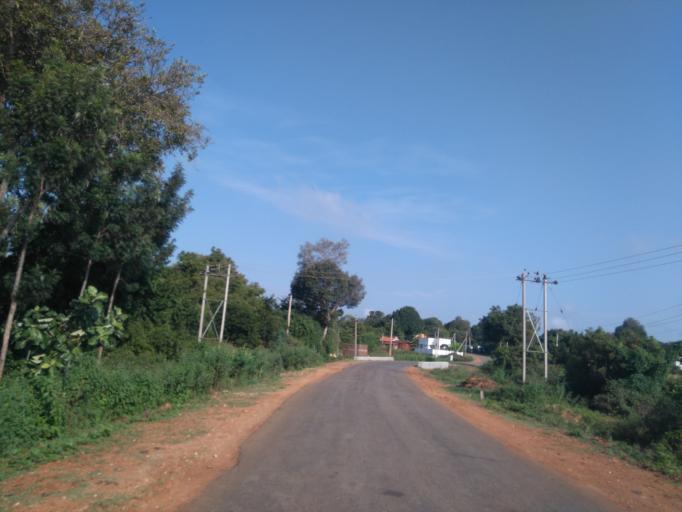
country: IN
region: Karnataka
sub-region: Chamrajnagar
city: Kollegal
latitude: 12.2608
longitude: 77.0428
